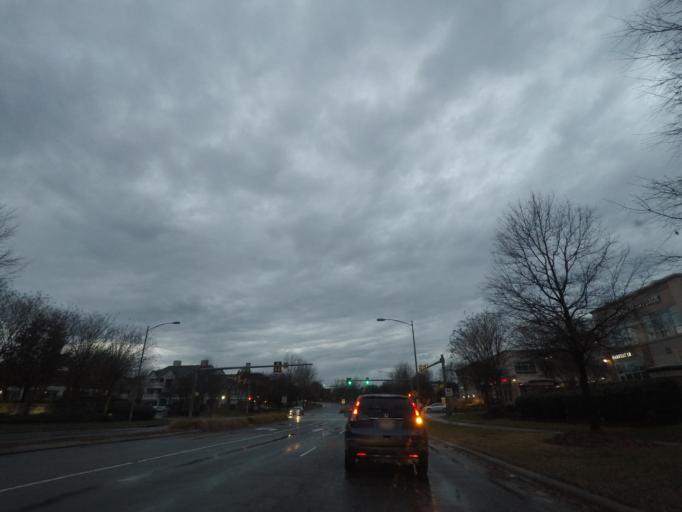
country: US
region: North Carolina
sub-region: Orange County
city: Chapel Hill
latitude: 35.9030
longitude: -78.9526
